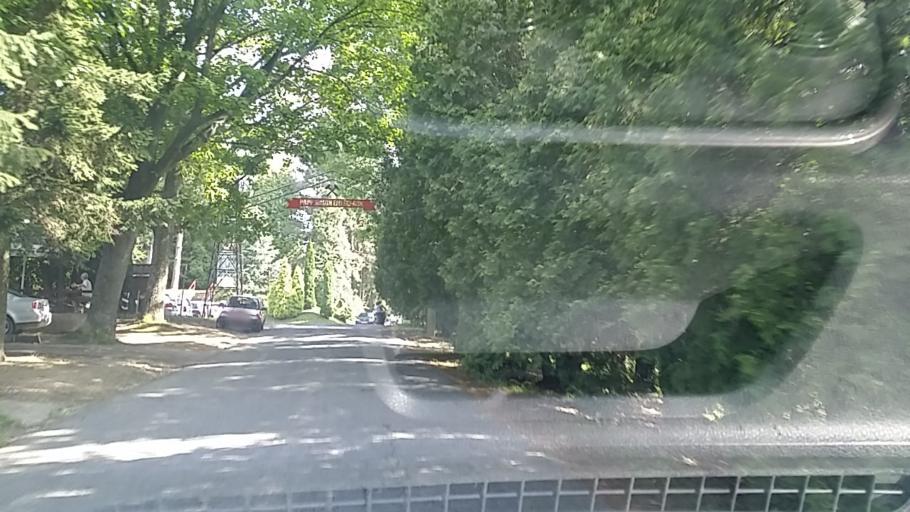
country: HU
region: Zala
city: Becsehely
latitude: 46.5207
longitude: 16.7355
